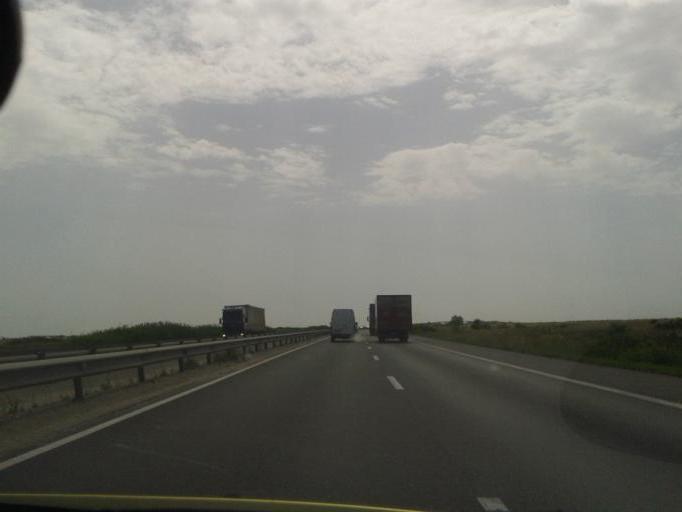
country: RO
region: Dambovita
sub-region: Comuna Petresti
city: Ionesti
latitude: 44.6956
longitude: 25.2497
